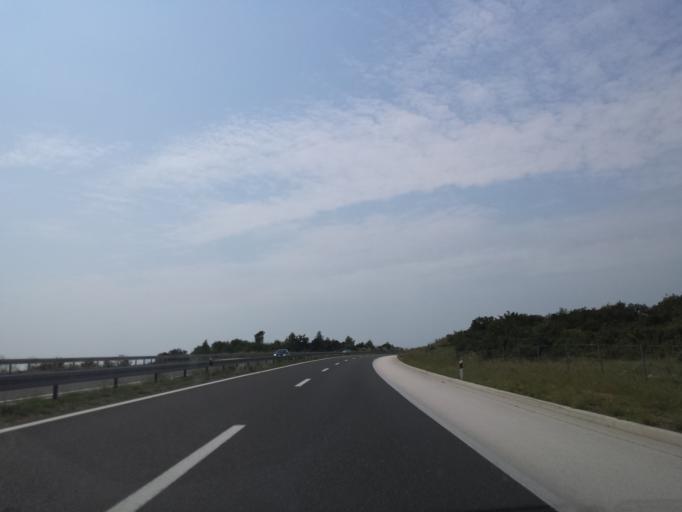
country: HR
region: Zadarska
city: Posedarje
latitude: 44.2197
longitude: 15.4992
